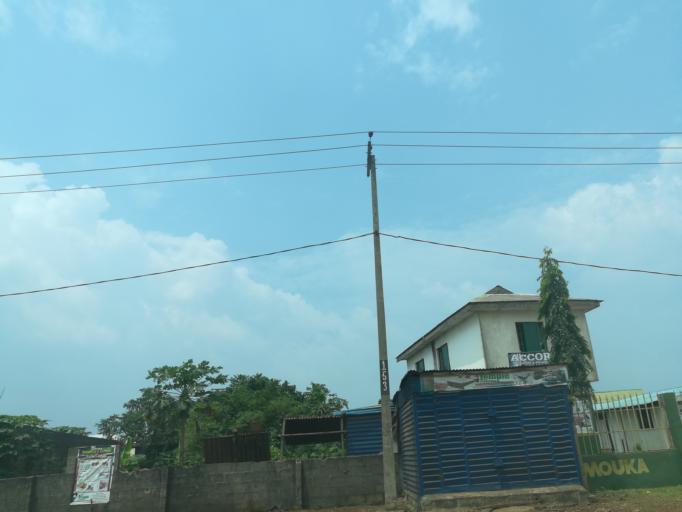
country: NG
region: Lagos
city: Ikorodu
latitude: 6.6072
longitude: 3.5945
